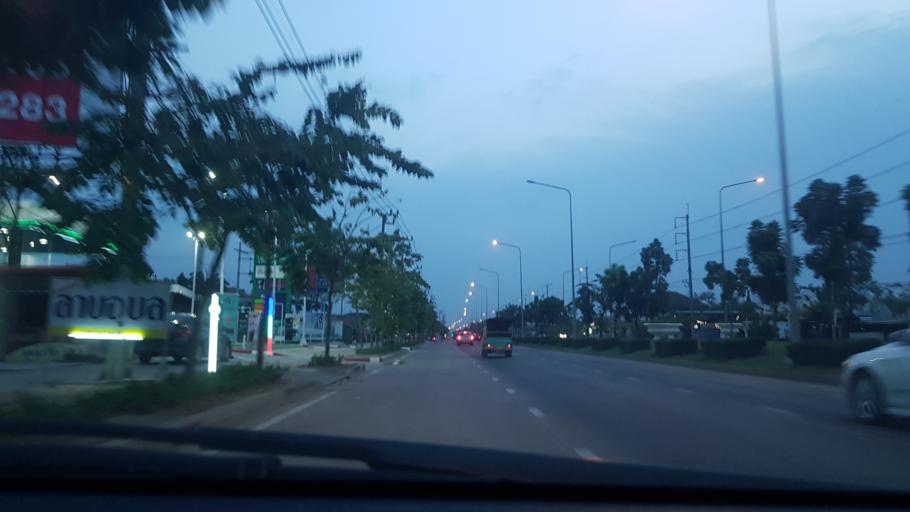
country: TH
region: Bangkok
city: Nong Khaem
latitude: 13.7425
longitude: 100.3640
